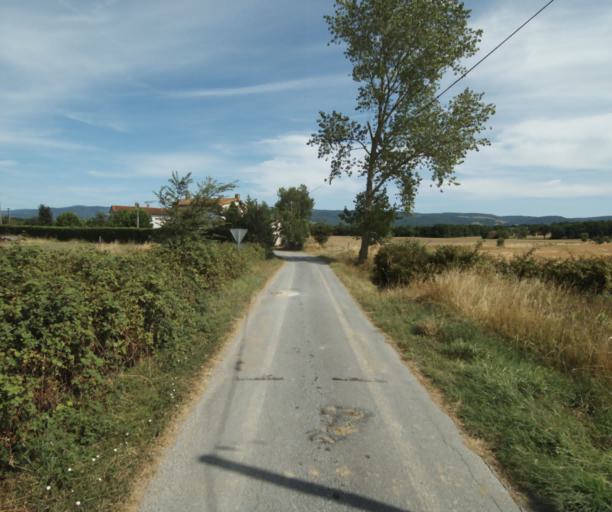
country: FR
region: Midi-Pyrenees
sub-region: Departement du Tarn
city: Soreze
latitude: 43.5045
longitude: 2.0560
